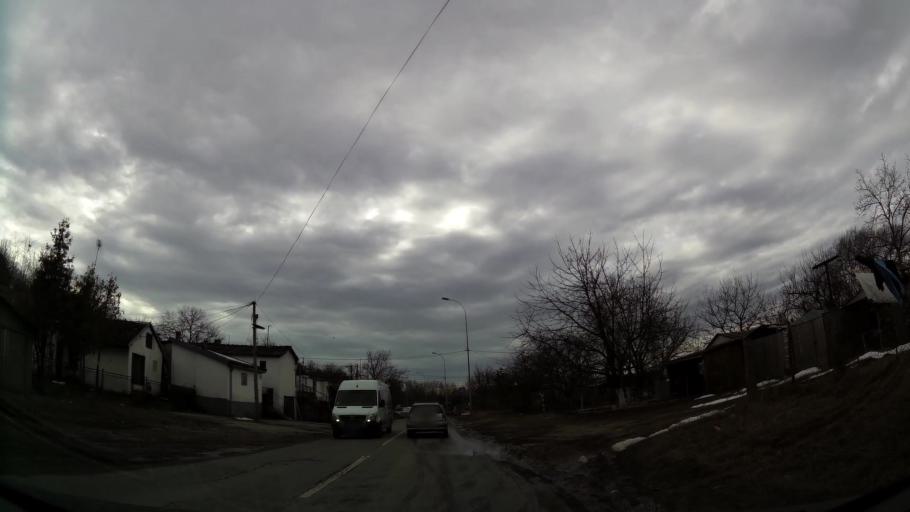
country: RS
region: Central Serbia
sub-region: Belgrade
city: Cukarica
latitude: 44.7610
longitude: 20.4040
